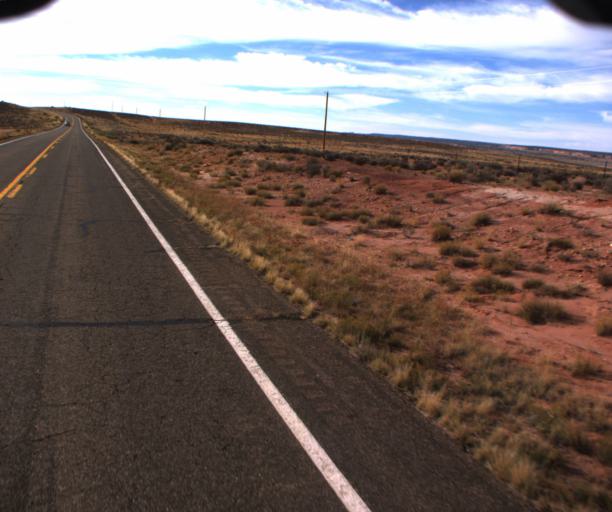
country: US
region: Arizona
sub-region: Coconino County
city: LeChee
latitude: 36.7385
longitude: -111.2846
